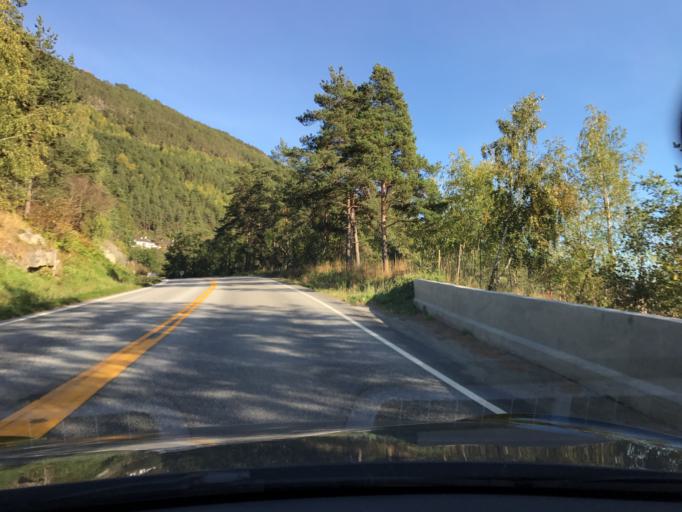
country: NO
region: Sogn og Fjordane
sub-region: Sogndal
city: Sogndalsfjora
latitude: 61.2121
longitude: 7.1343
